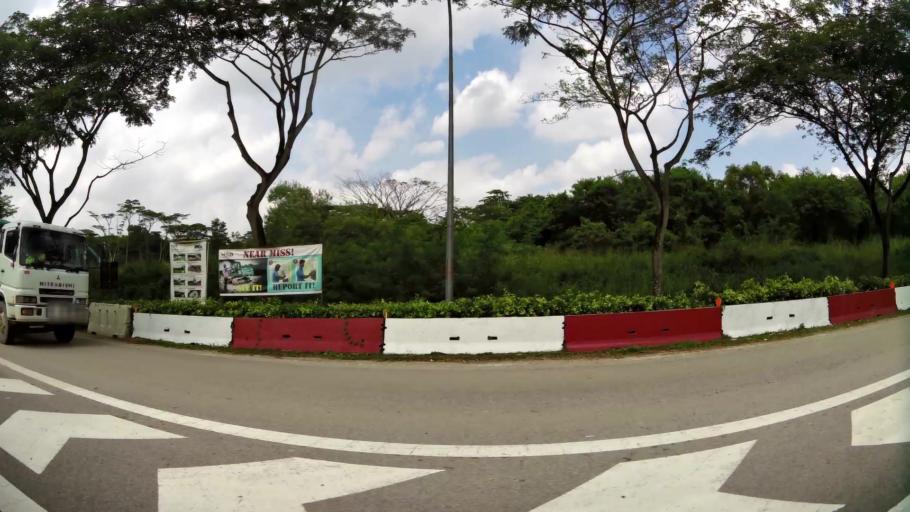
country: MY
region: Johor
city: Kampung Pasir Gudang Baru
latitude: 1.3798
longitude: 103.9152
